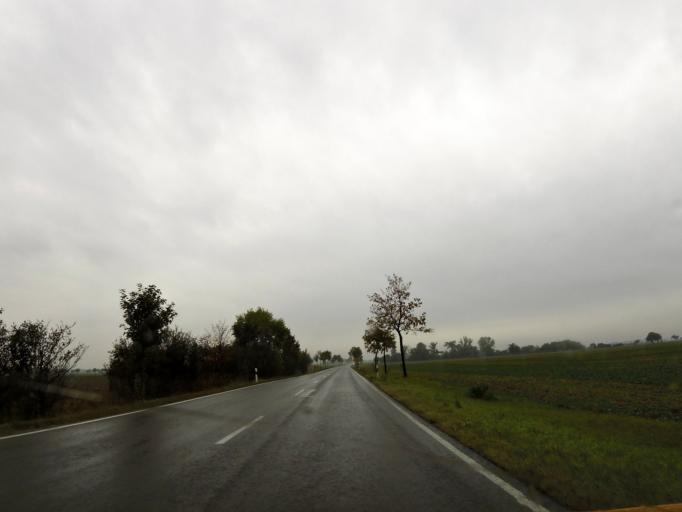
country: DE
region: Saxony-Anhalt
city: Osternienburg
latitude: 51.7808
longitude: 12.0762
